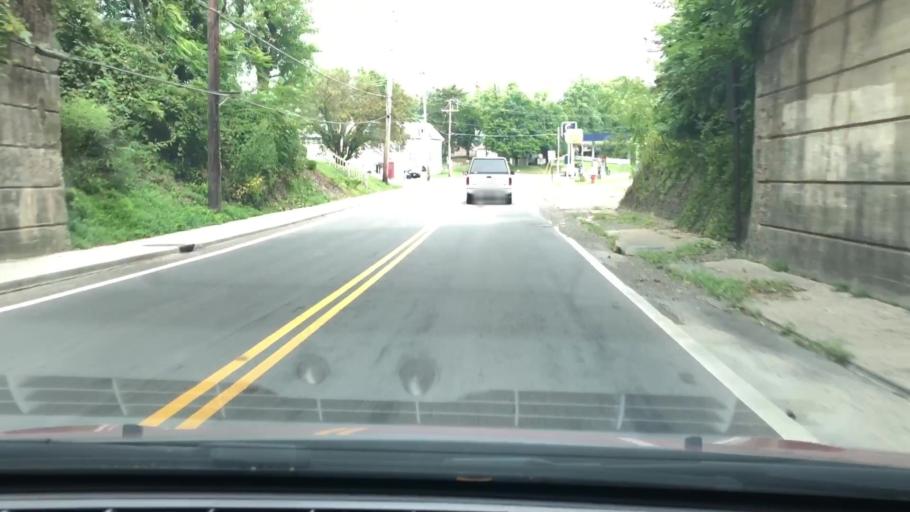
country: US
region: Ohio
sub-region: Delaware County
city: Sunbury
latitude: 40.2407
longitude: -82.8560
